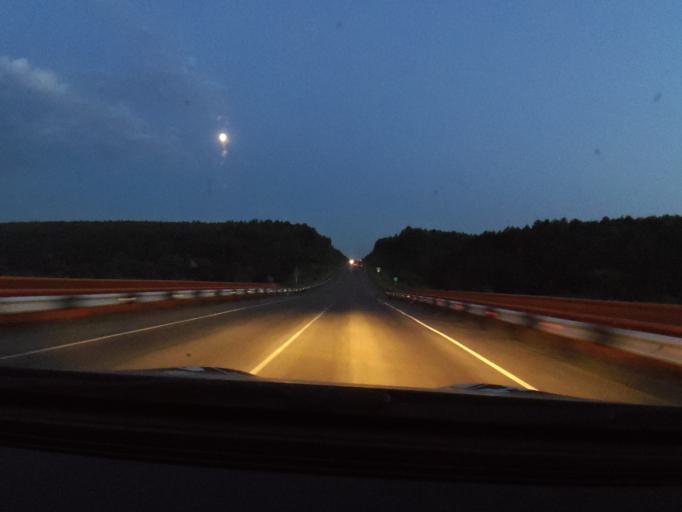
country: RU
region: Bashkortostan
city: Duvan
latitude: 55.9666
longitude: 58.2026
